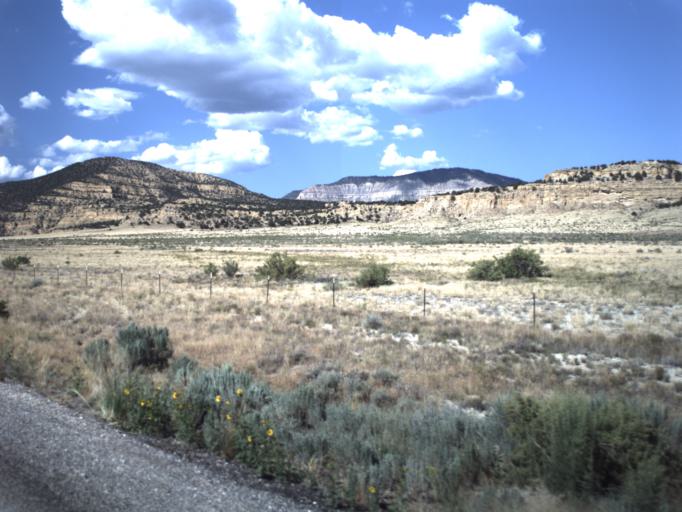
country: US
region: Utah
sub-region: Emery County
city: Ferron
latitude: 38.8010
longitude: -111.3414
